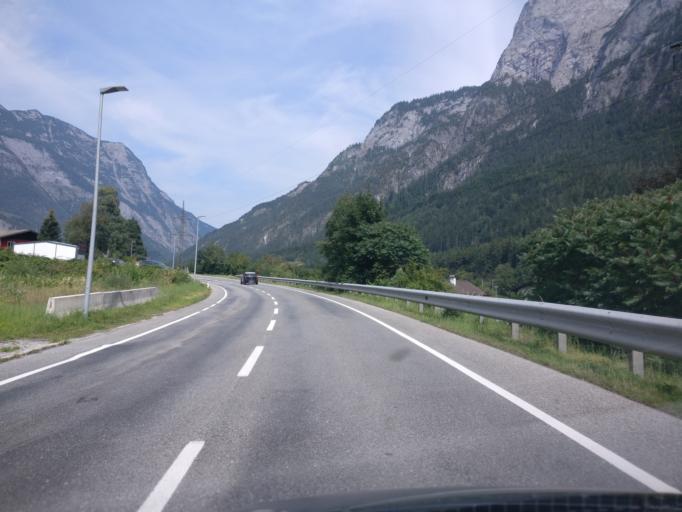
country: AT
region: Salzburg
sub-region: Politischer Bezirk Sankt Johann im Pongau
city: Werfen
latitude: 47.4956
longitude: 13.1760
